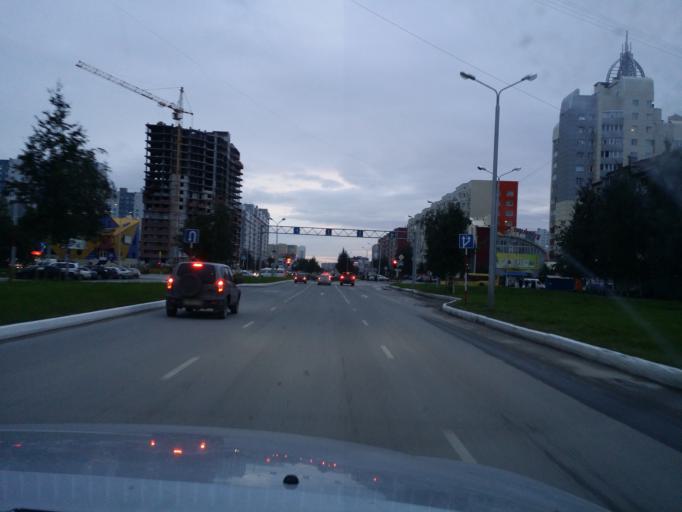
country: RU
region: Khanty-Mansiyskiy Avtonomnyy Okrug
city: Nizhnevartovsk
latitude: 60.9320
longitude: 76.6014
